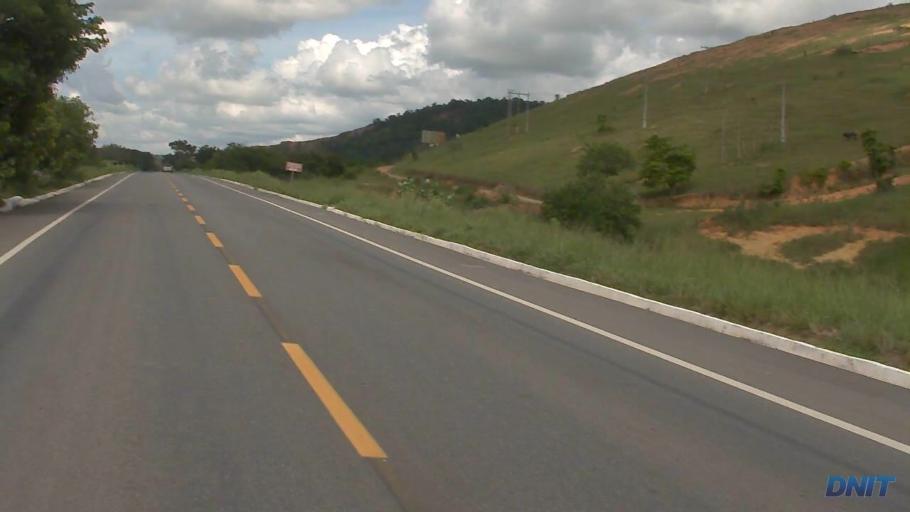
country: BR
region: Minas Gerais
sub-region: Governador Valadares
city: Governador Valadares
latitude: -18.9446
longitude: -42.0648
